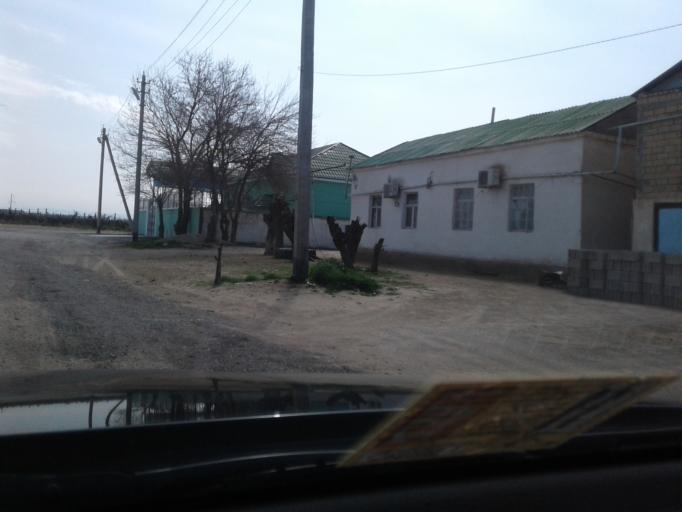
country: TM
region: Ahal
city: Abadan
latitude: 38.1182
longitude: 58.3519
